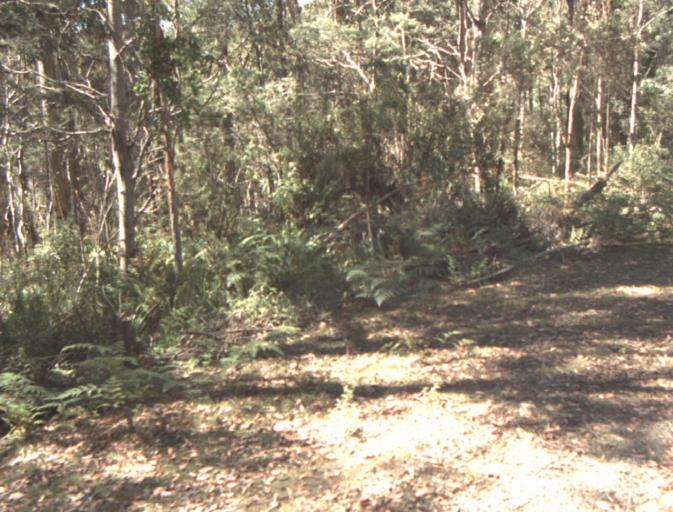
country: AU
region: Tasmania
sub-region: Dorset
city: Scottsdale
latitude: -41.3784
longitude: 147.4859
